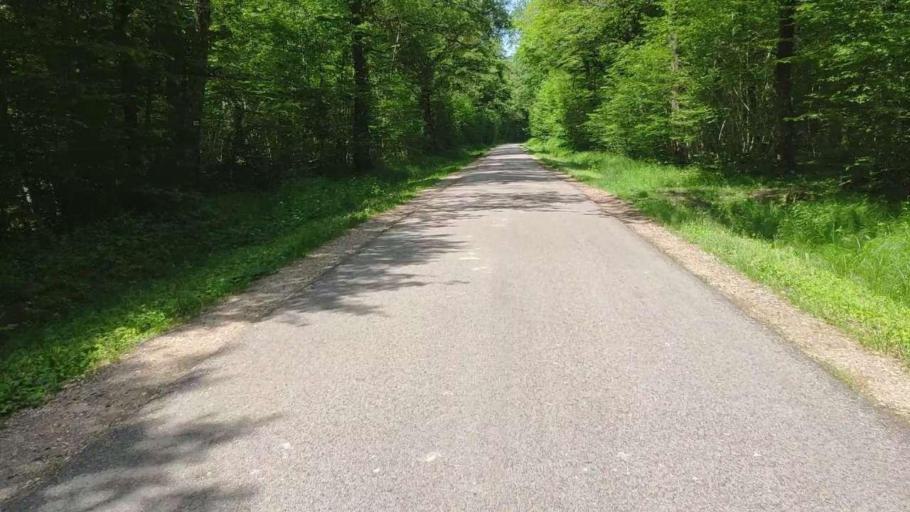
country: FR
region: Franche-Comte
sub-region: Departement du Jura
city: Bletterans
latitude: 46.7583
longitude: 5.4398
